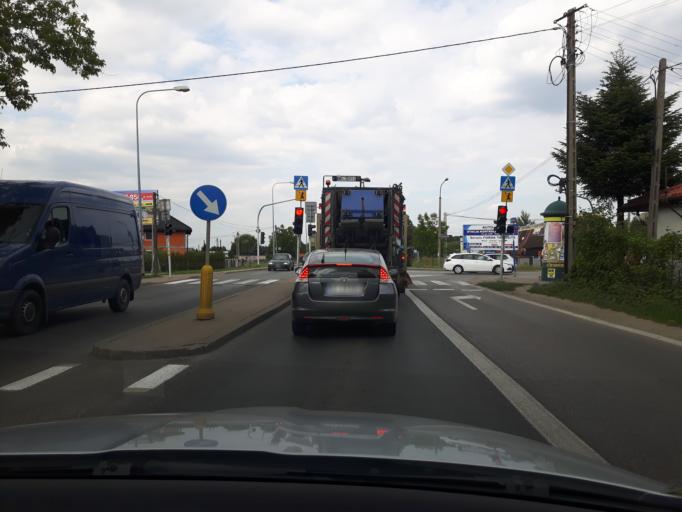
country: PL
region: Masovian Voivodeship
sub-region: Powiat legionowski
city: Stanislawow Pierwszy
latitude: 52.3554
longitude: 21.0284
